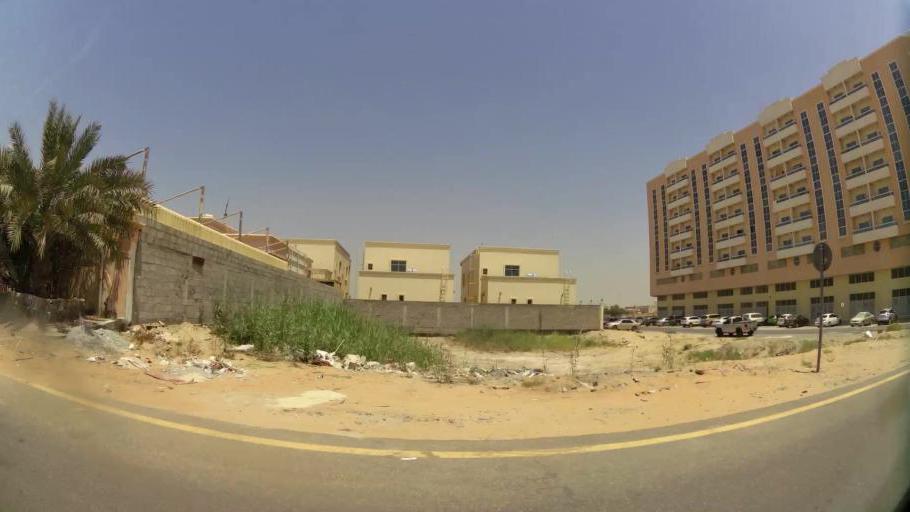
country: AE
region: Ajman
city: Ajman
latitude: 25.4096
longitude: 55.5165
